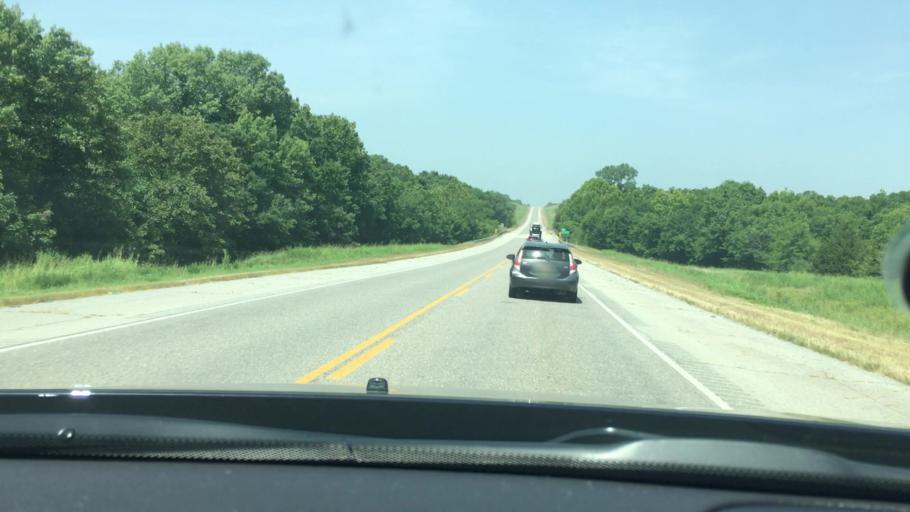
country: US
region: Oklahoma
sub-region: Coal County
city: Coalgate
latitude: 34.6110
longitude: -96.3911
